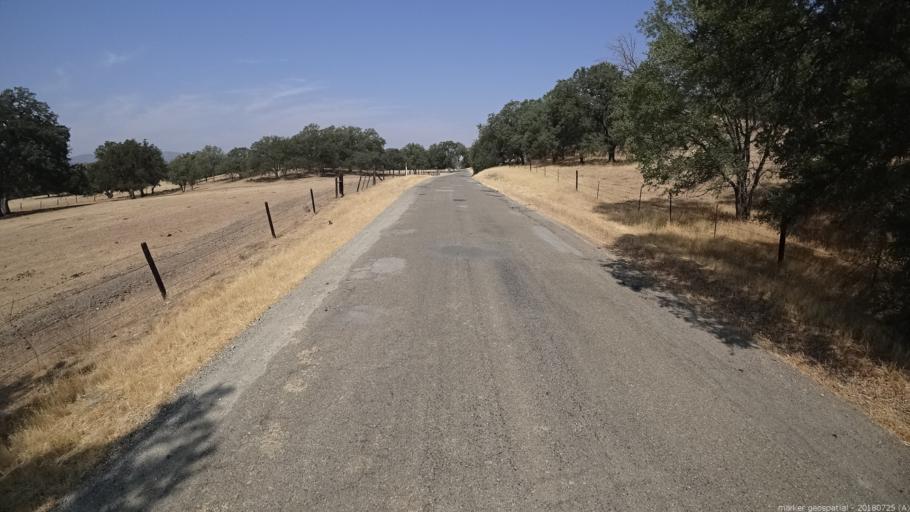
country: US
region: California
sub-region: San Luis Obispo County
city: Shandon
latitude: 35.8740
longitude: -120.4126
